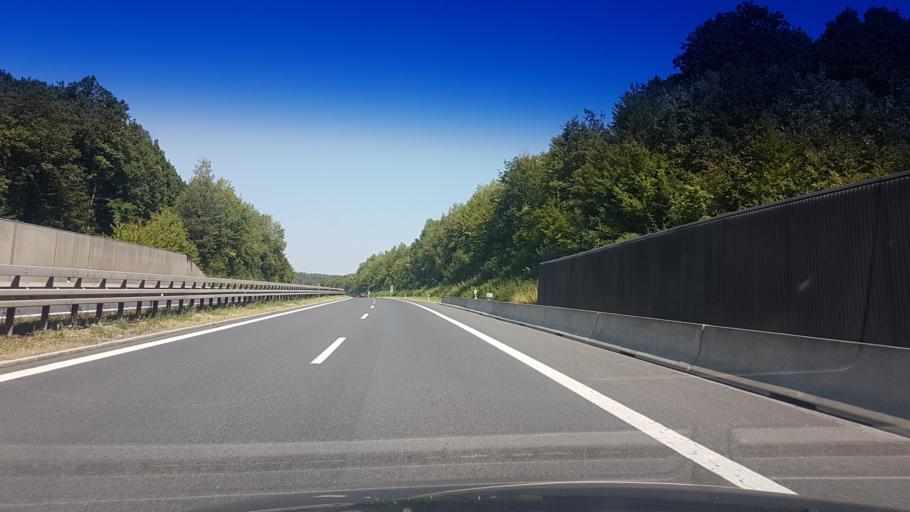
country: DE
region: Bavaria
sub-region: Upper Franconia
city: Zapfendorf
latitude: 50.0085
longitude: 10.9375
